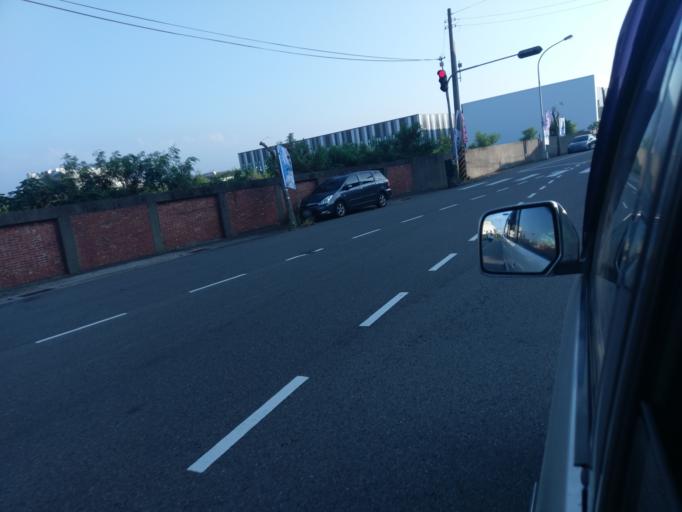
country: TW
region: Taiwan
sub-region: Miaoli
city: Miaoli
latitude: 24.6789
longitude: 120.8780
